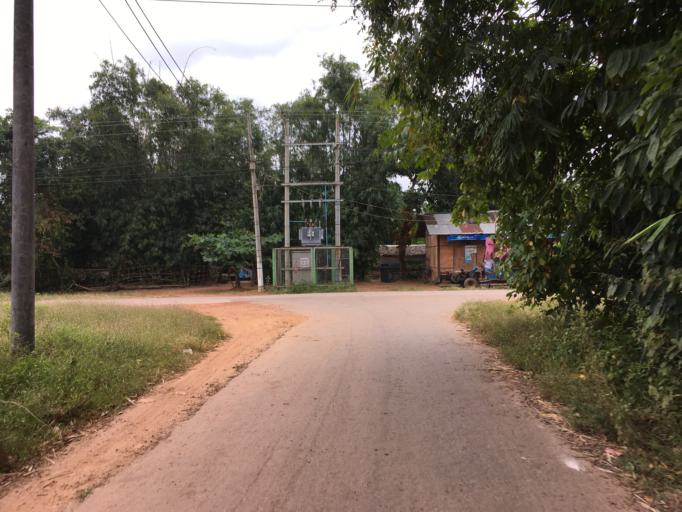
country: MM
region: Mon
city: Mawlamyine
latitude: 16.4286
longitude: 97.6284
